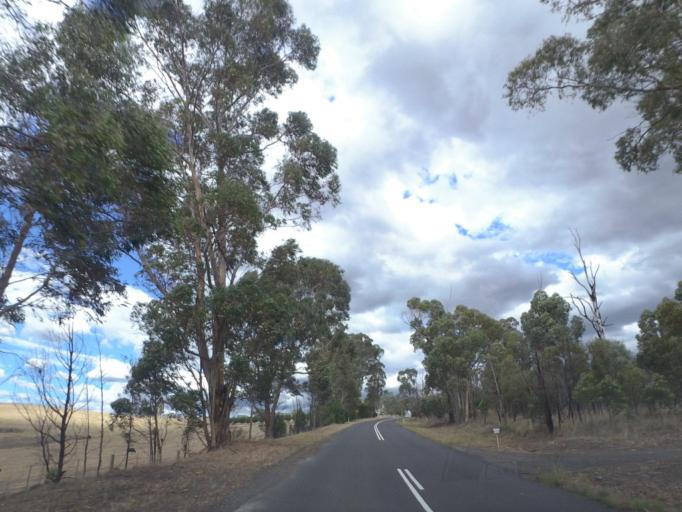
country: AU
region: Victoria
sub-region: Yarra Ranges
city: Healesville
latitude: -37.6435
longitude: 145.4556
